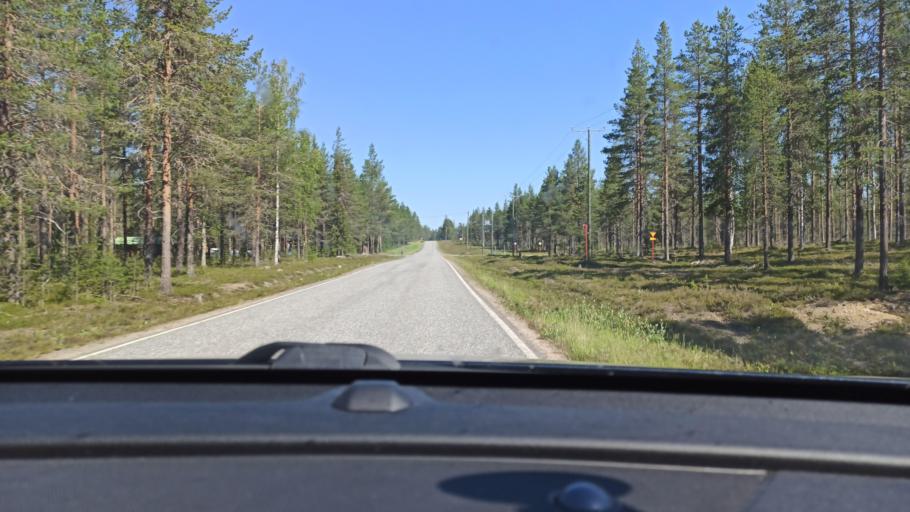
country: FI
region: Lapland
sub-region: Tunturi-Lappi
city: Kolari
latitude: 67.6513
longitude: 24.1623
